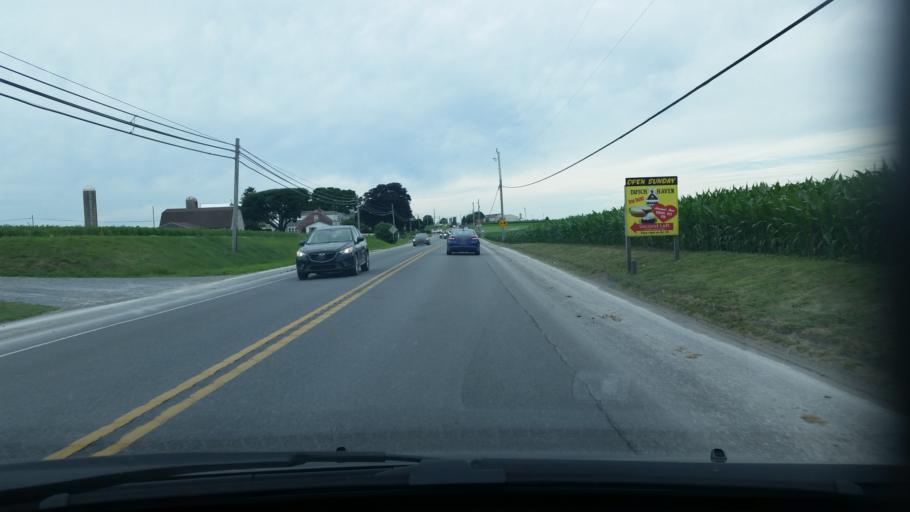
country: US
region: Pennsylvania
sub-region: Lancaster County
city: Intercourse
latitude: 40.0393
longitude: -76.1149
